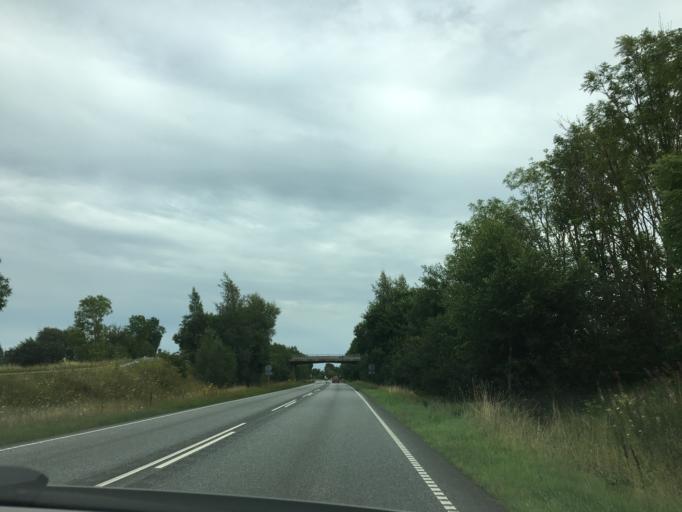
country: DK
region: South Denmark
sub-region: Vejle Kommune
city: Brejning
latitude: 55.6342
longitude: 9.6842
